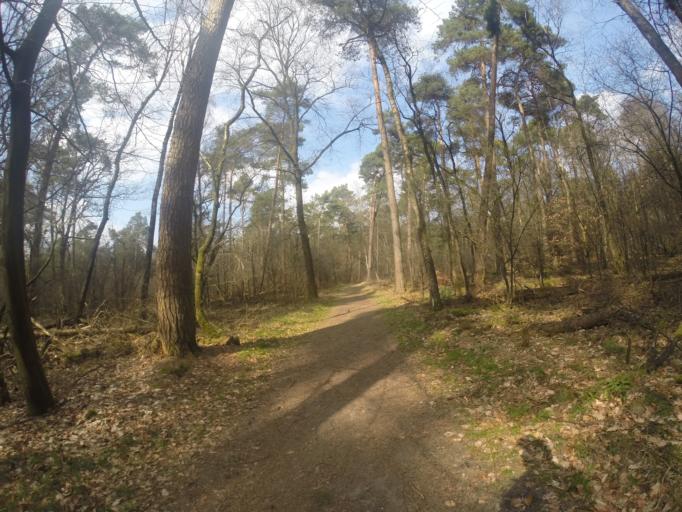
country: NL
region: Gelderland
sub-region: Gemeente Lochem
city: Almen
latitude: 52.1505
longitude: 6.3280
